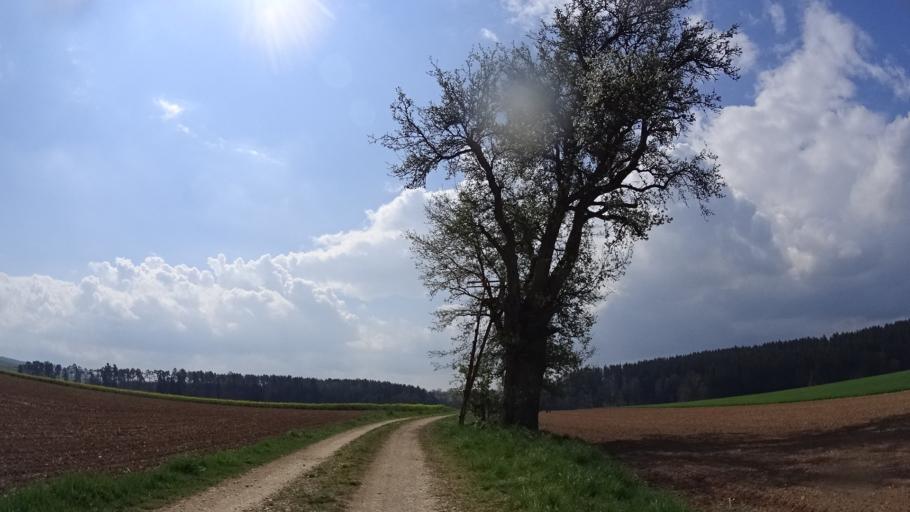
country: DE
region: Bavaria
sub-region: Upper Bavaria
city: Hitzhofen
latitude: 48.8675
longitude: 11.3110
